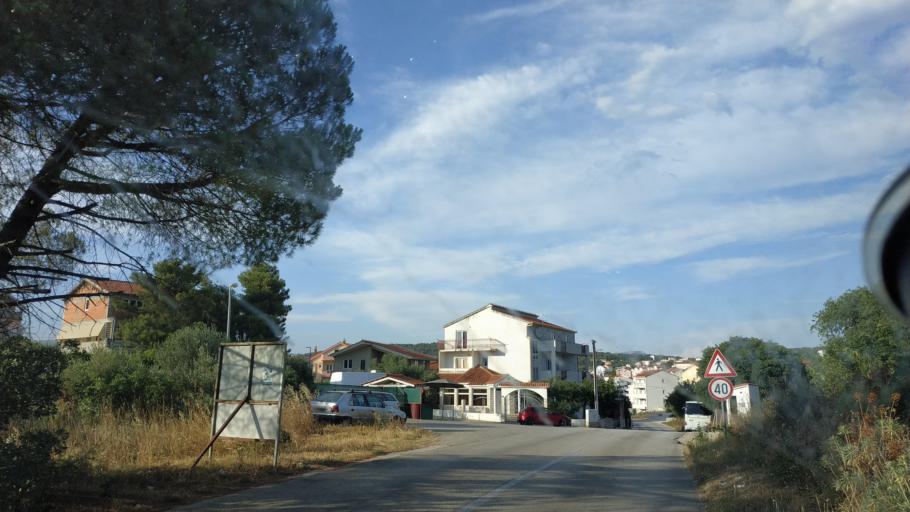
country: HR
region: Splitsko-Dalmatinska
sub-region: Grad Trogir
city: Trogir
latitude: 43.4896
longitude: 16.2532
